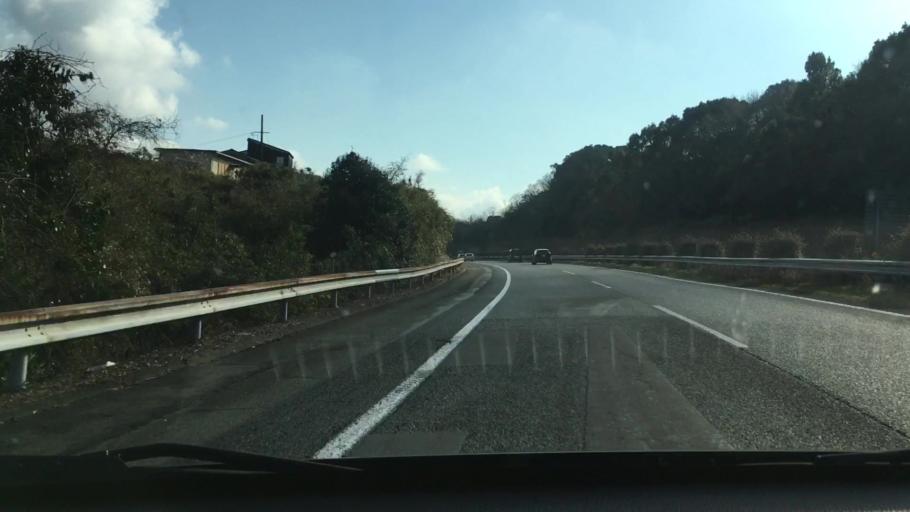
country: JP
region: Kumamoto
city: Matsubase
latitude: 32.6427
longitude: 130.7066
